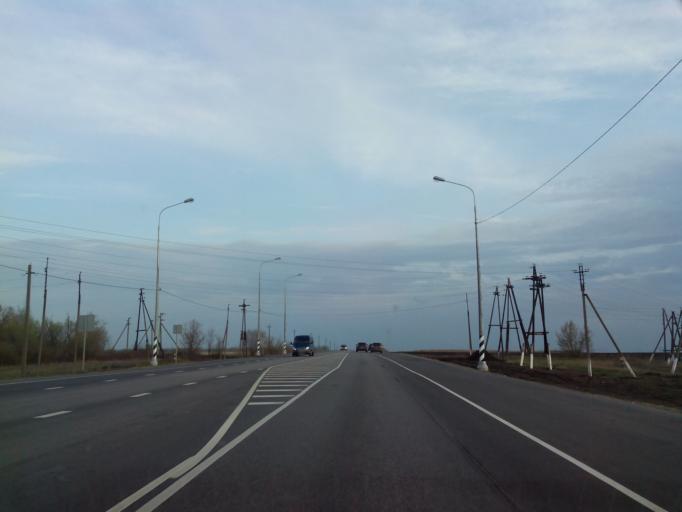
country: RU
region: Rjazan
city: Ryazhsk
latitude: 53.5901
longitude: 40.0380
